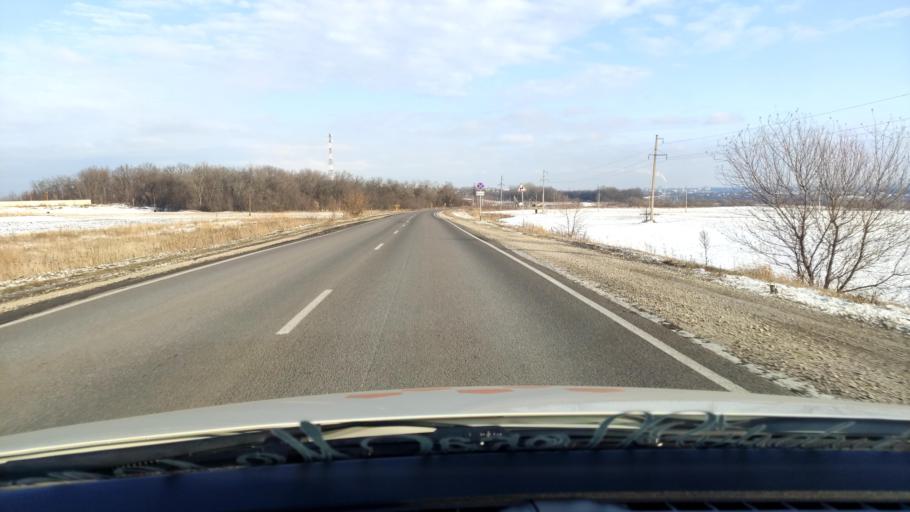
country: RU
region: Voronezj
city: Devitsa
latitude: 51.6829
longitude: 38.9690
